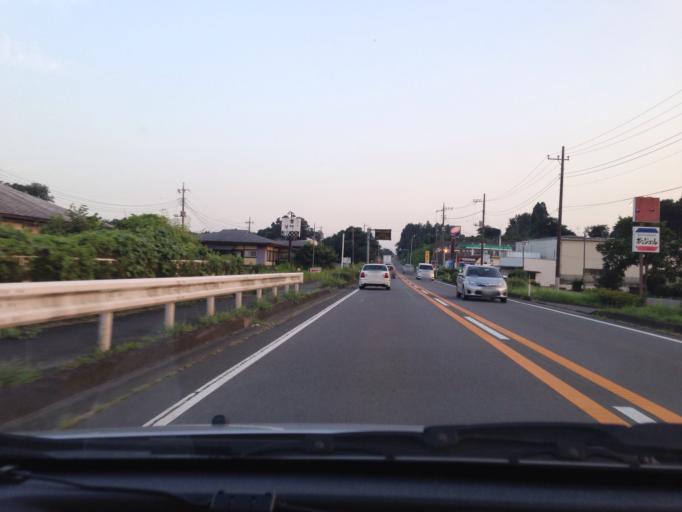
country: JP
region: Ibaraki
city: Ishioka
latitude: 36.1488
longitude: 140.2385
